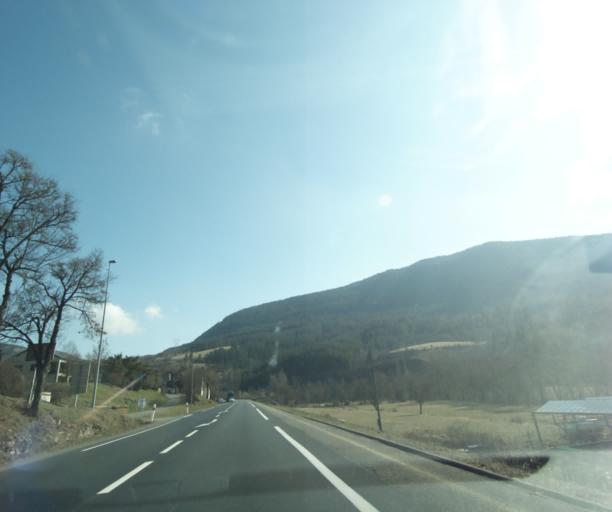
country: FR
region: Languedoc-Roussillon
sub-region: Departement de la Lozere
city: Mende
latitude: 44.5251
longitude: 3.5176
